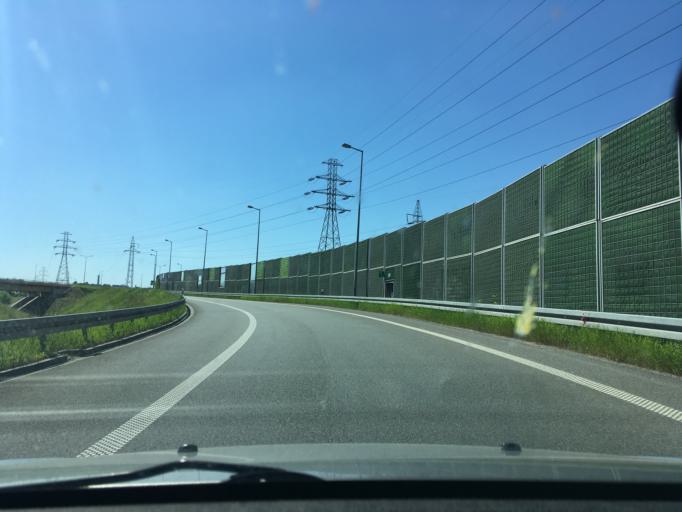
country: PL
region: Lesser Poland Voivodeship
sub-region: Powiat wielicki
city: Czarnochowice
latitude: 50.0058
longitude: 20.0224
